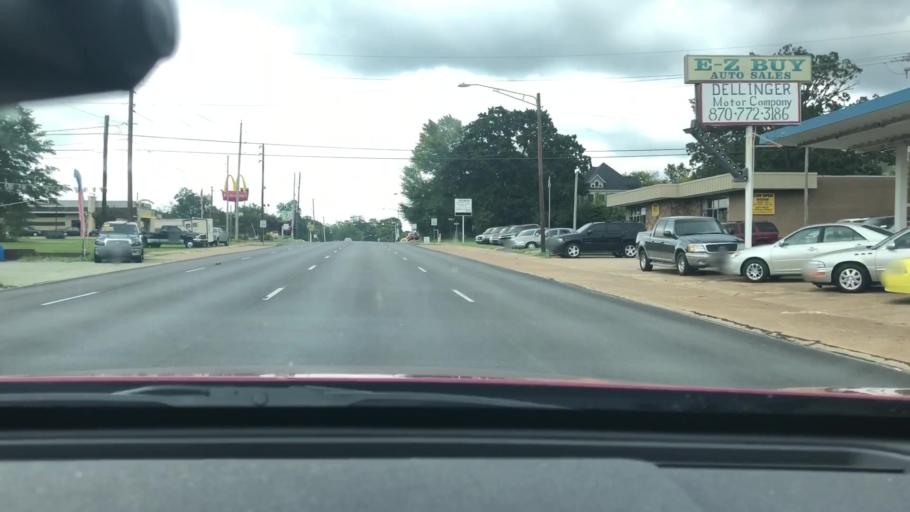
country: US
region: Texas
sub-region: Bowie County
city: Texarkana
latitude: 33.4295
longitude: -94.0382
